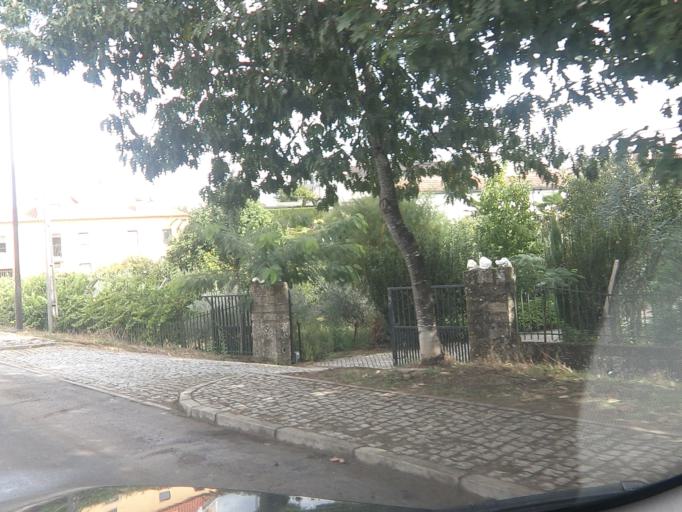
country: PT
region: Vila Real
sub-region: Vila Real
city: Vila Real
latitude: 41.2911
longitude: -7.7288
